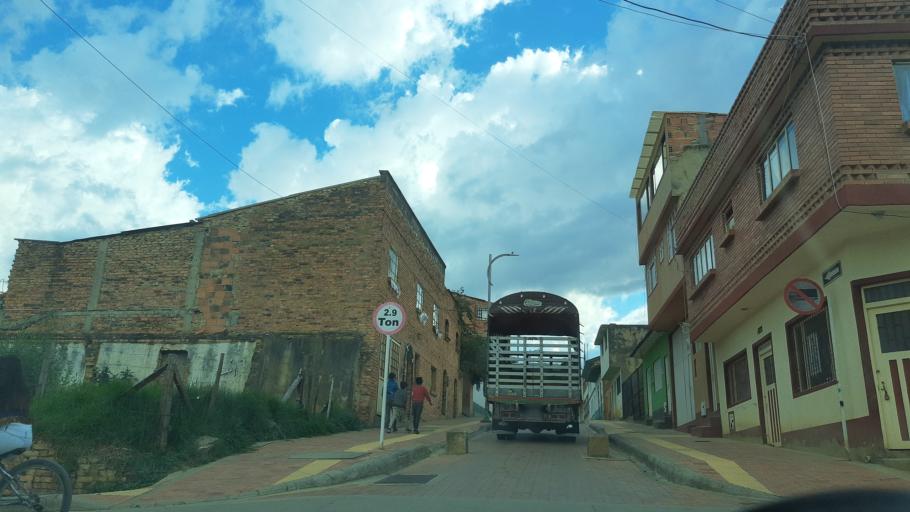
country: CO
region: Boyaca
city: Santa Sofia
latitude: 5.7147
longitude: -73.6016
